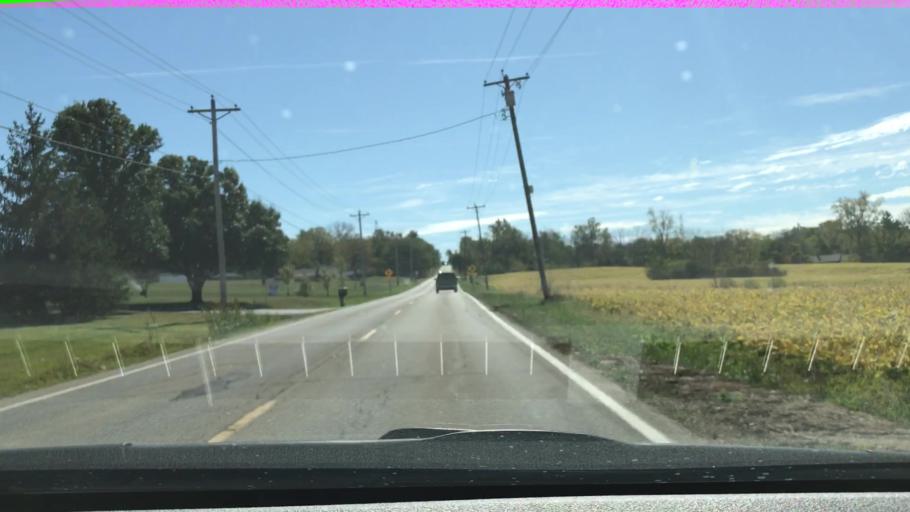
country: US
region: Ohio
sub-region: Butler County
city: Hamilton
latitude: 39.4554
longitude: -84.6246
